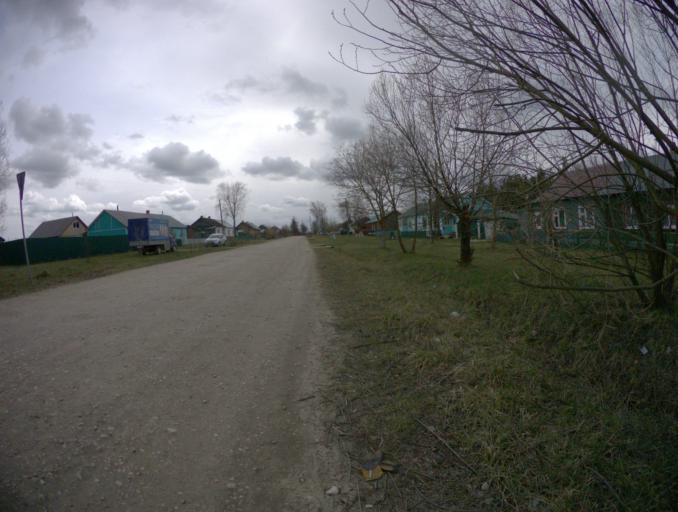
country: RU
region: Vladimir
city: Sudogda
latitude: 56.0696
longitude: 40.7949
